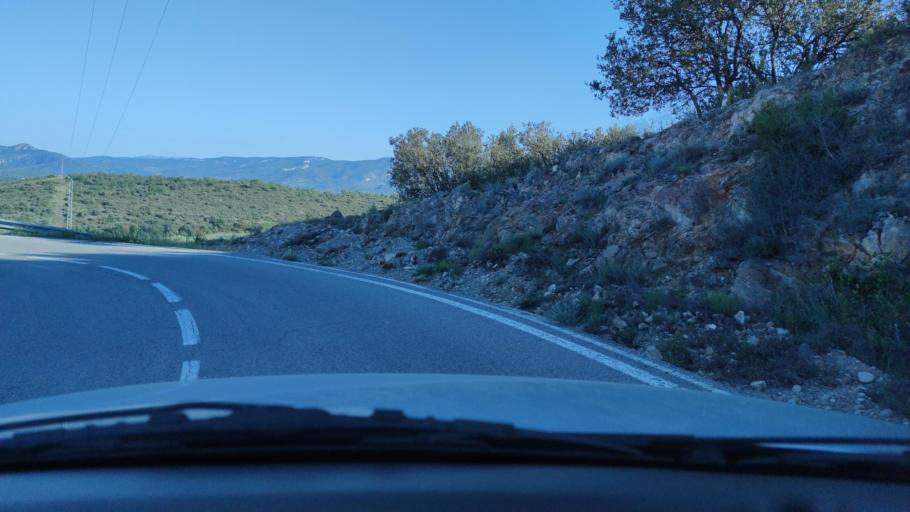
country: ES
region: Catalonia
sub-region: Provincia de Lleida
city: Artesa de Segre
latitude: 41.8831
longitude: 1.0061
